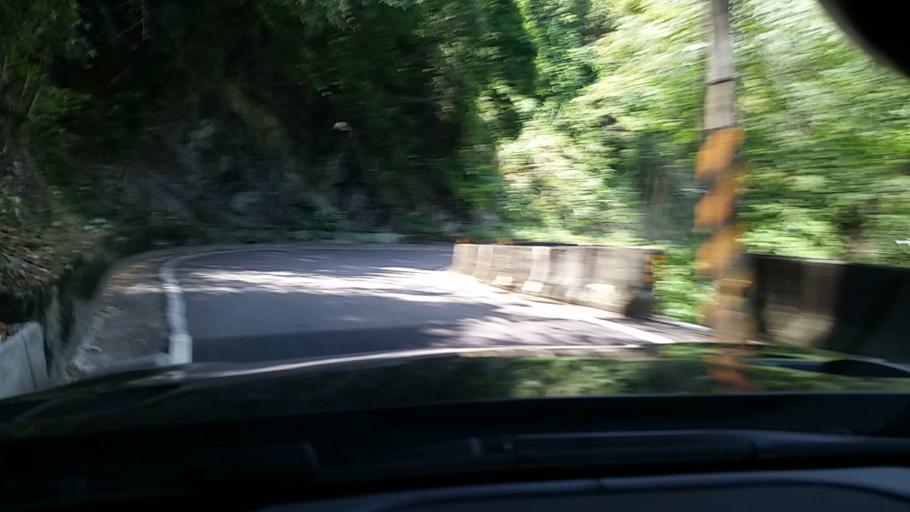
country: TW
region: Taiwan
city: Daxi
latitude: 24.7121
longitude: 121.3616
